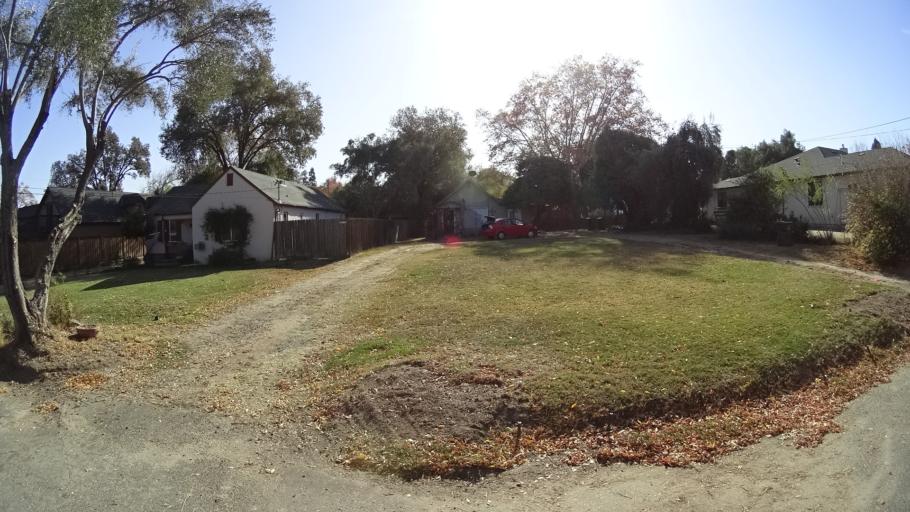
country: US
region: California
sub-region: Sacramento County
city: Citrus Heights
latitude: 38.7065
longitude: -121.2864
